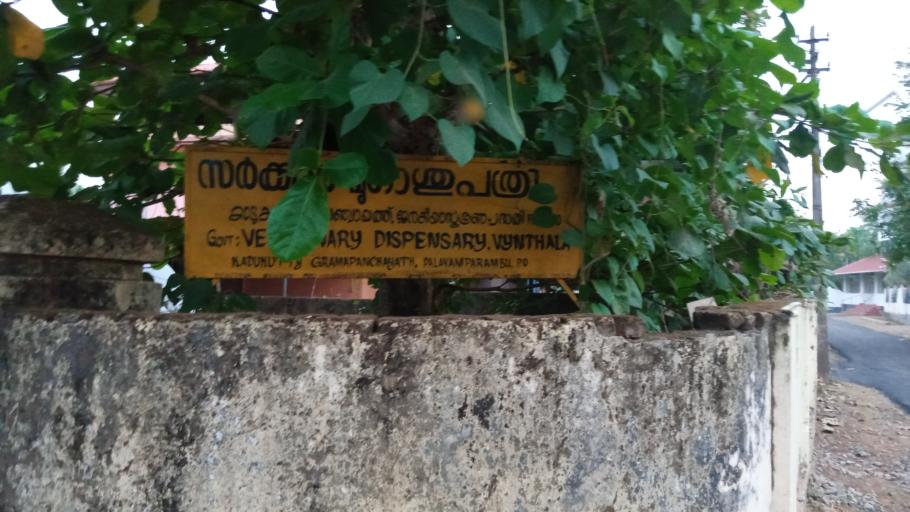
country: IN
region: Kerala
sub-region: Thrissur District
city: Kizhake Chalakudi
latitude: 10.2591
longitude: 76.3029
